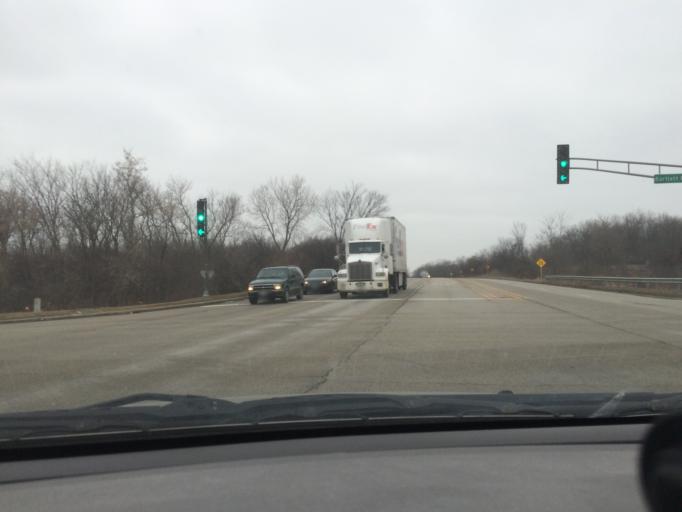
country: US
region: Illinois
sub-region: Cook County
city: Streamwood
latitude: 42.0463
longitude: -88.1789
